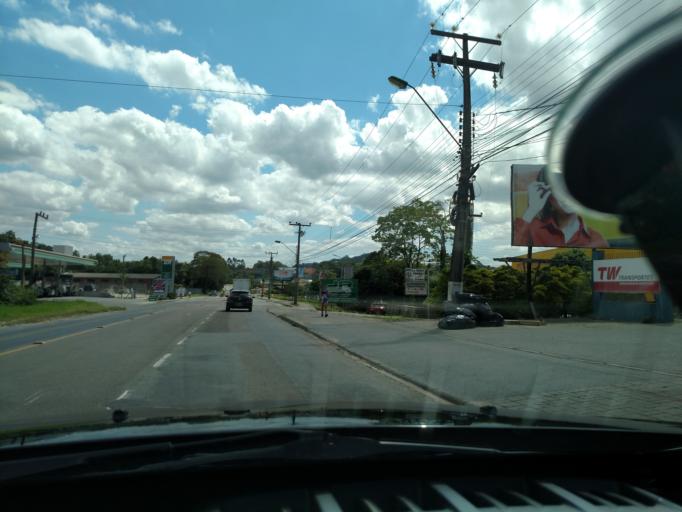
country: BR
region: Santa Catarina
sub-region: Blumenau
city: Blumenau
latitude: -26.8727
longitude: -49.1004
